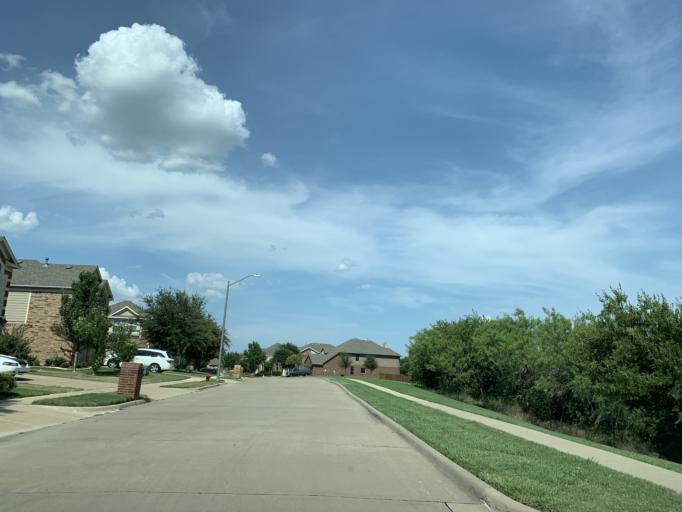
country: US
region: Texas
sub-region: Dallas County
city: Cedar Hill
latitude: 32.6498
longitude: -97.0010
